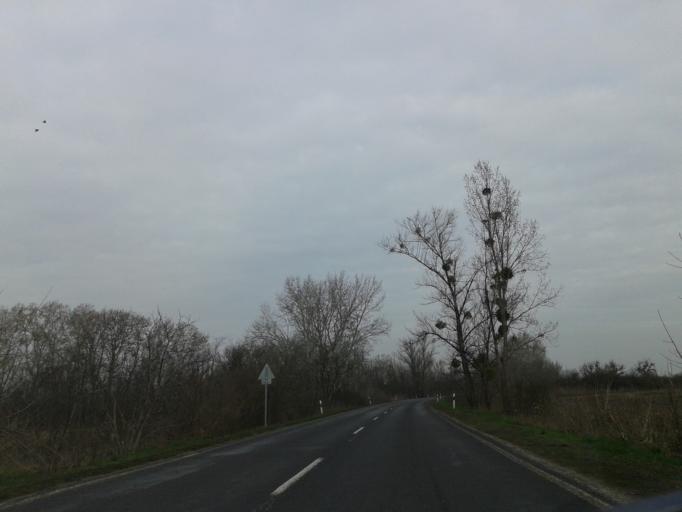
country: HU
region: Komarom-Esztergom
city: Dunaalmas
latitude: 47.6997
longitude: 18.3008
